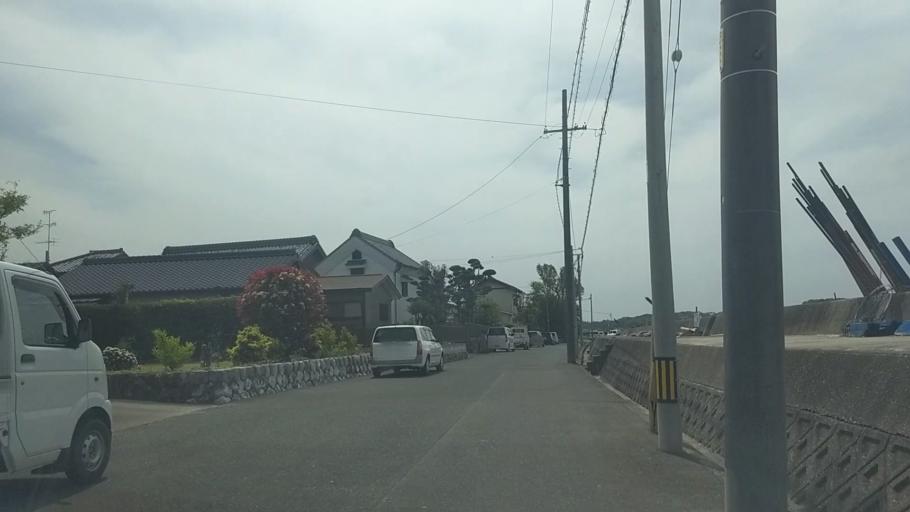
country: JP
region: Shizuoka
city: Kosai-shi
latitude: 34.7334
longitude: 137.5381
